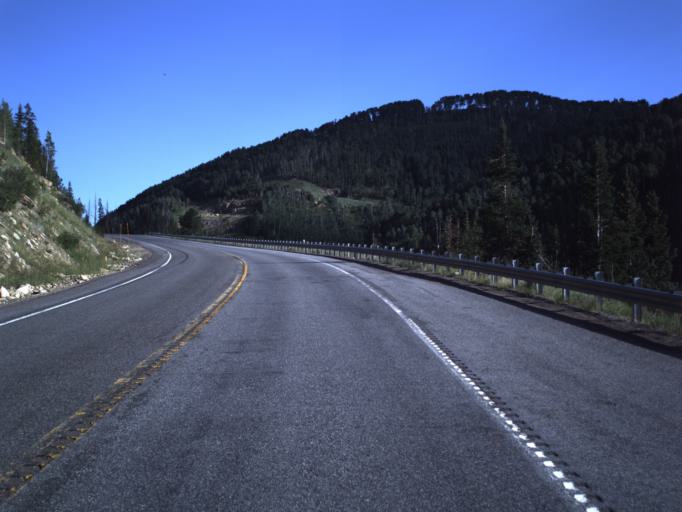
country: US
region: Utah
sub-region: Sanpete County
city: Fairview
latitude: 39.5957
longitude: -111.2060
